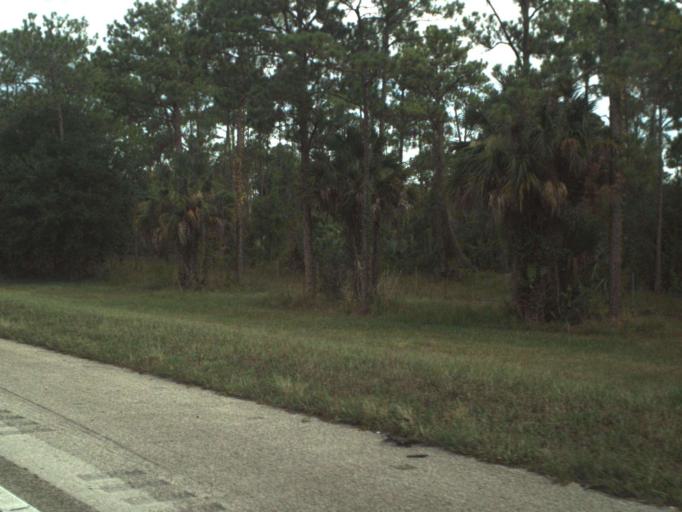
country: US
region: Florida
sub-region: Martin County
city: Palm City
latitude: 27.1278
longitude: -80.3405
